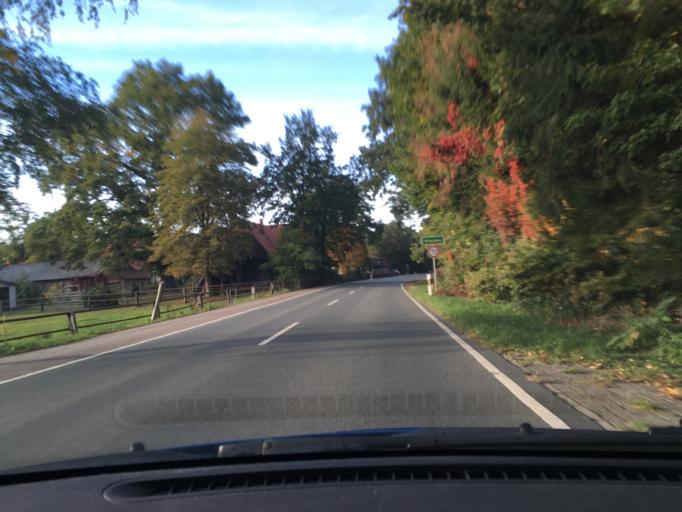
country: DE
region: Lower Saxony
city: Fassberg
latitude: 52.9172
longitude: 10.1279
